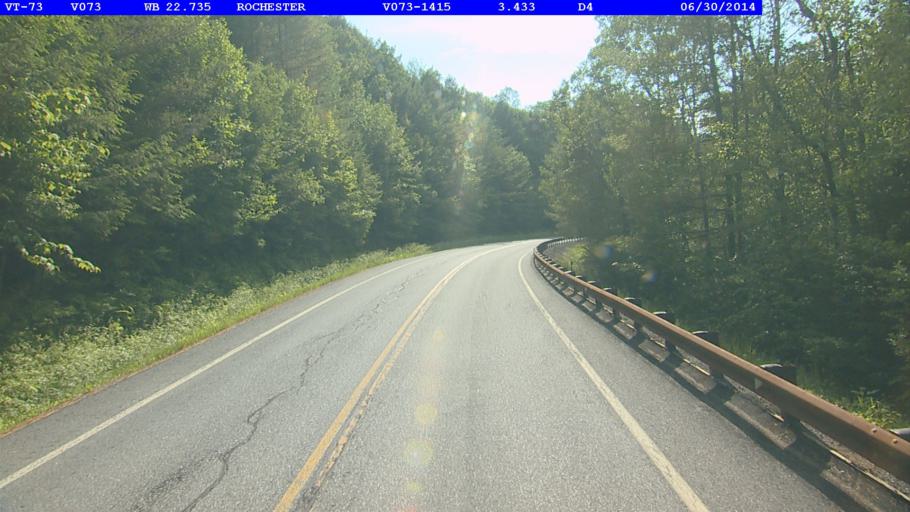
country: US
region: Vermont
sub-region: Rutland County
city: Brandon
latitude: 43.8518
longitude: -72.9025
